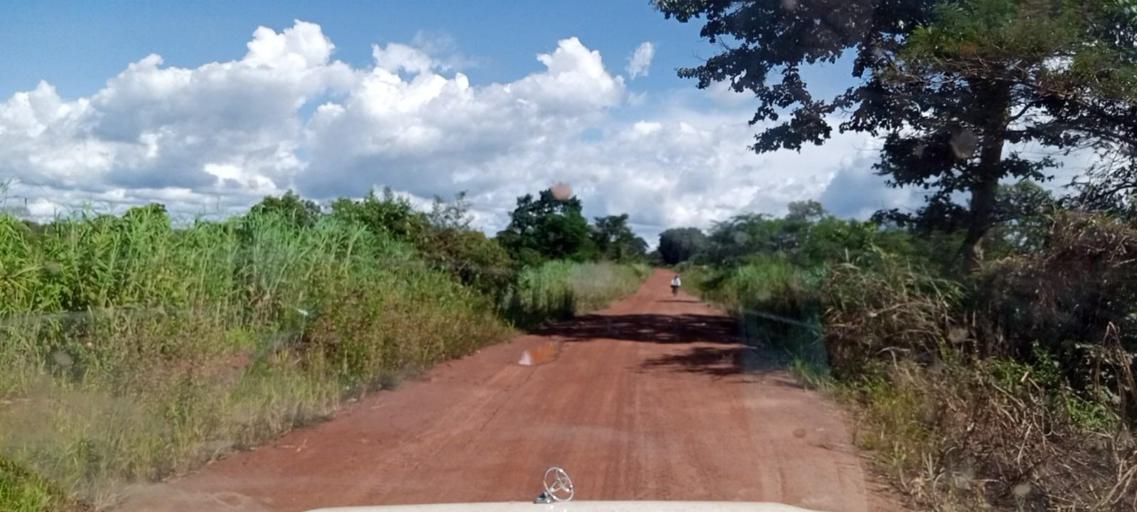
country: ZM
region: Luapula
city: Mwense
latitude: -10.2459
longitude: 28.1027
